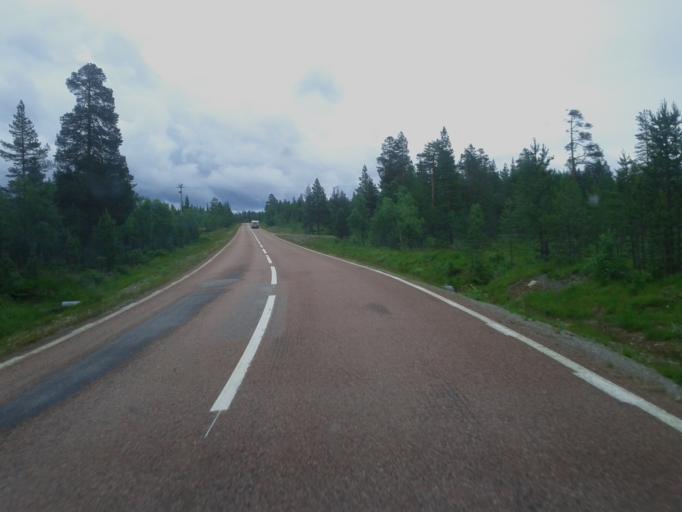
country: NO
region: Hedmark
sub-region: Engerdal
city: Engerdal
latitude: 61.8036
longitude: 12.3736
